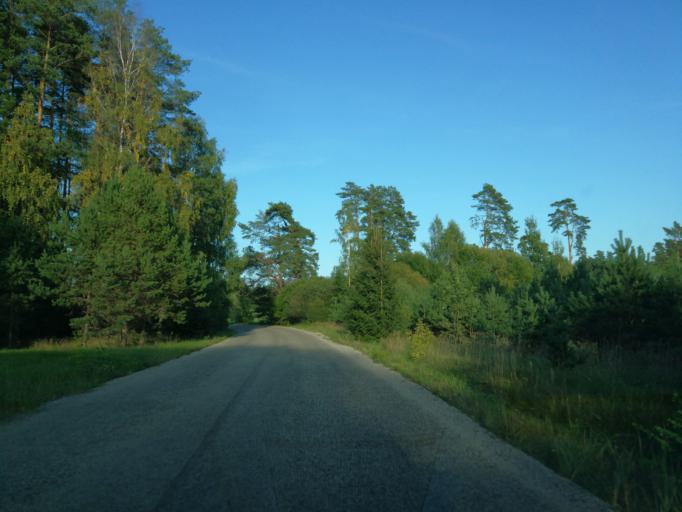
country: LV
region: Garkalne
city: Garkalne
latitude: 57.0823
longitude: 24.4678
